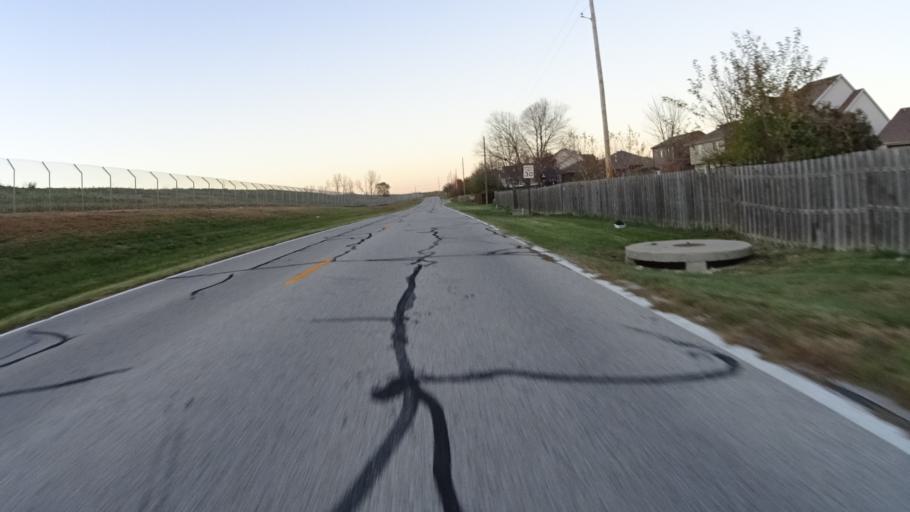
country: US
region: Nebraska
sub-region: Sarpy County
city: Offutt Air Force Base
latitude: 41.1627
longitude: -95.9560
